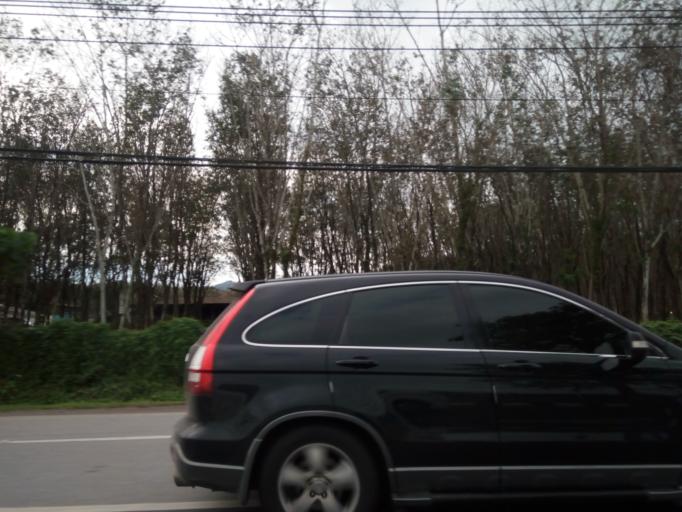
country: TH
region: Phuket
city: Thalang
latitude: 8.0495
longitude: 98.3377
